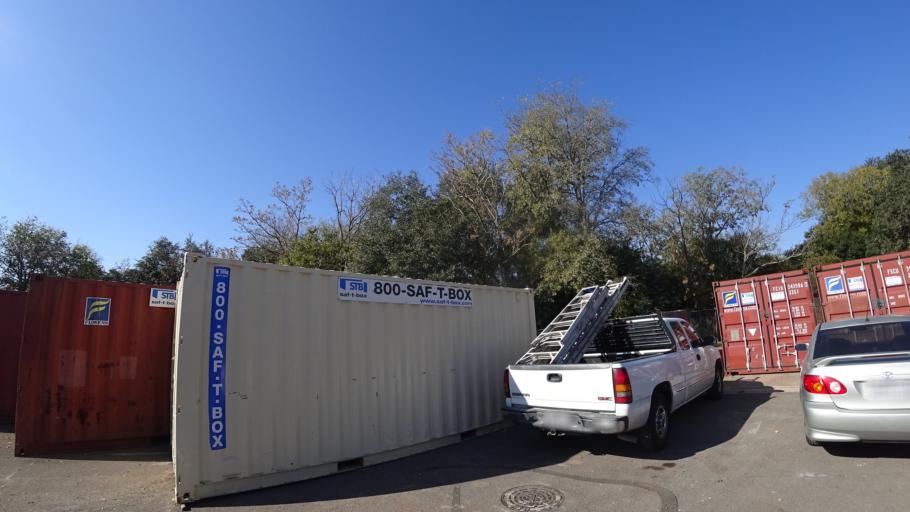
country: US
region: Texas
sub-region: Travis County
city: Barton Creek
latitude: 30.2344
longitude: -97.8531
